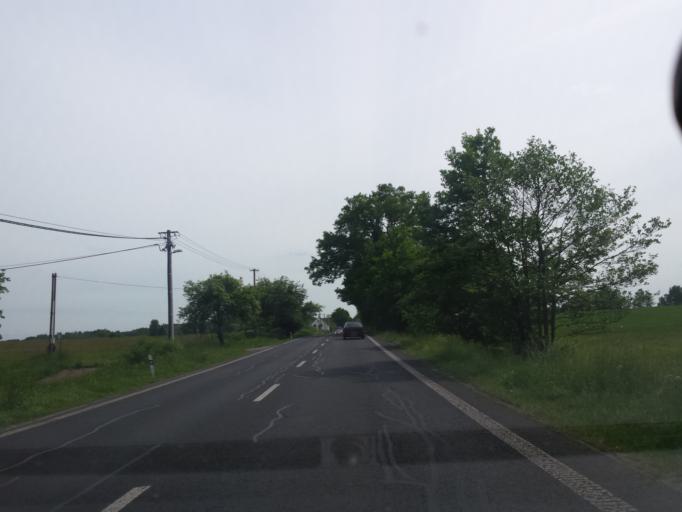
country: CZ
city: Novy Bor
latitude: 50.7255
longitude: 14.5460
